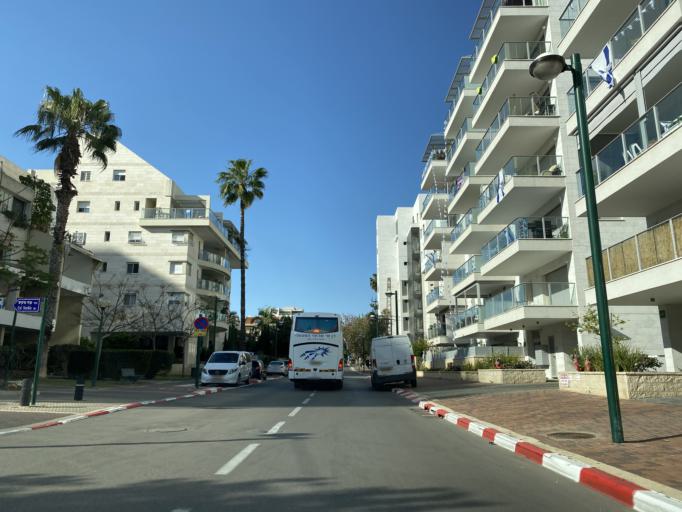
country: IL
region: Central District
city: Kfar Saba
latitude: 32.1775
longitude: 34.9151
